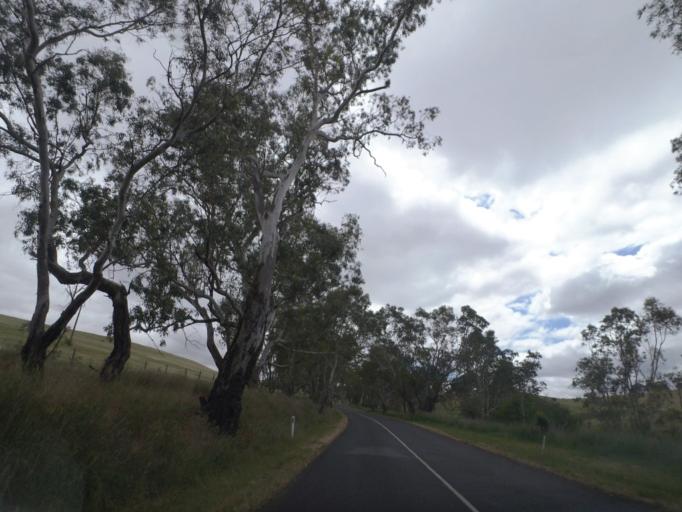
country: AU
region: Victoria
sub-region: Whittlesea
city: Whittlesea
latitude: -37.1939
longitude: 145.0383
